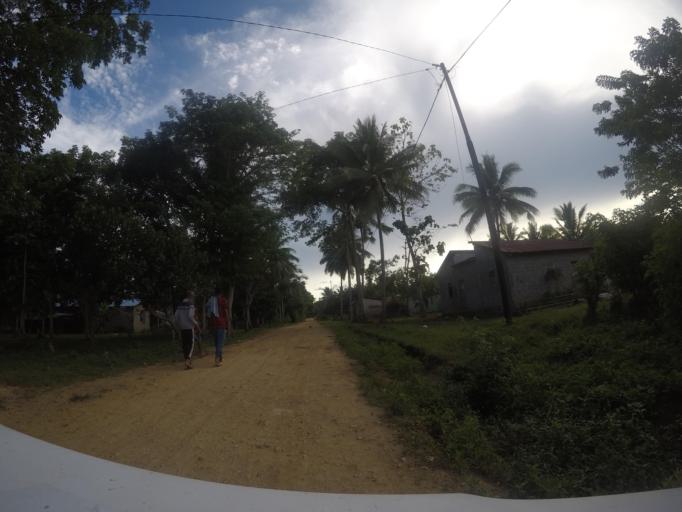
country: TL
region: Lautem
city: Lospalos
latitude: -8.4996
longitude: 126.9977
